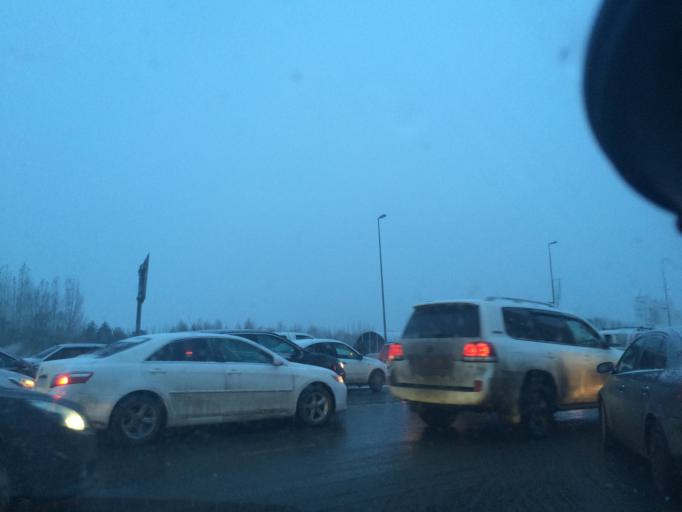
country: KZ
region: Astana Qalasy
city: Astana
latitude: 51.1537
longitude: 71.4304
